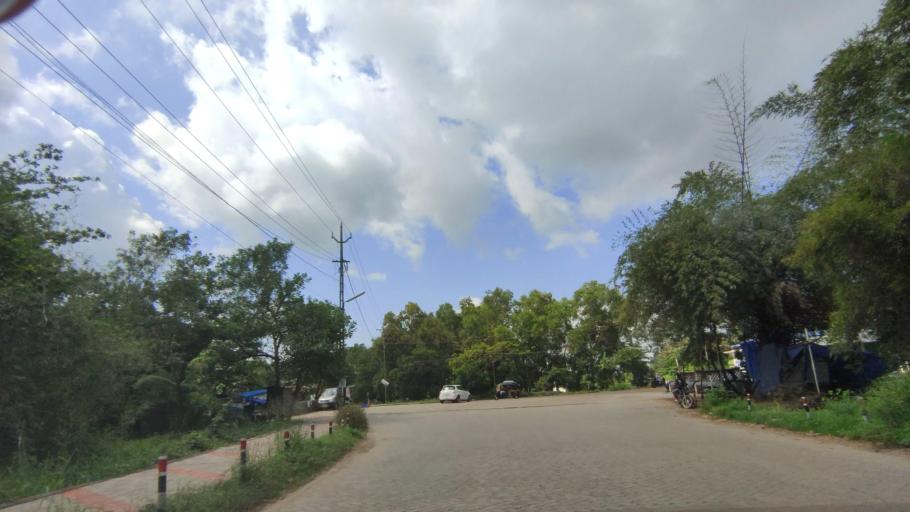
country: IN
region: Kerala
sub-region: Kottayam
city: Kottayam
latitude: 9.5667
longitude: 76.5207
